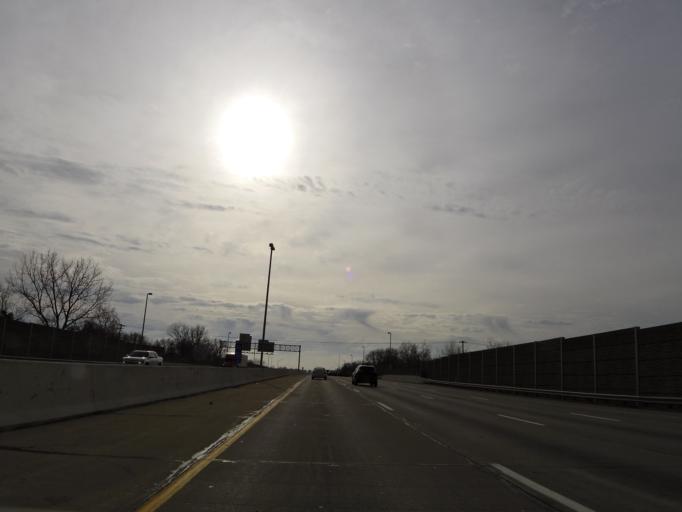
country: US
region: Indiana
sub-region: Marion County
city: Warren Park
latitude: 39.7827
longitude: -86.0319
